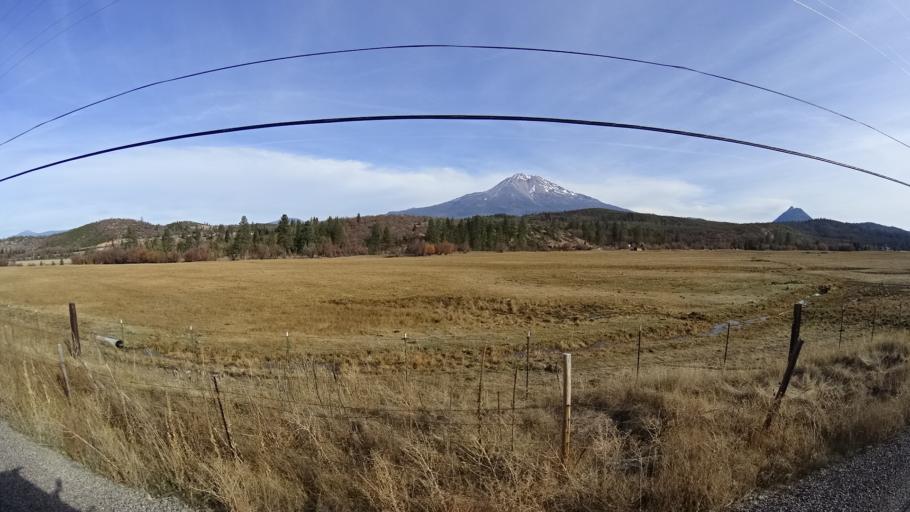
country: US
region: California
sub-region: Siskiyou County
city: Weed
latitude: 41.4281
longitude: -122.4373
